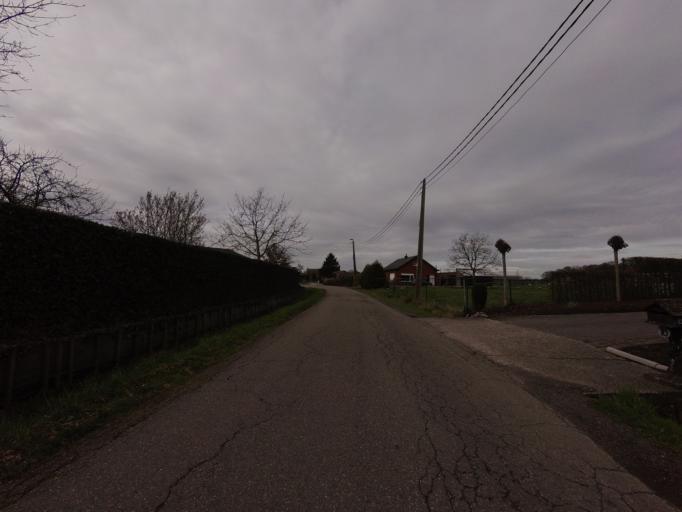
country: BE
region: Flanders
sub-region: Provincie Antwerpen
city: Lint
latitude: 51.1369
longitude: 4.5286
